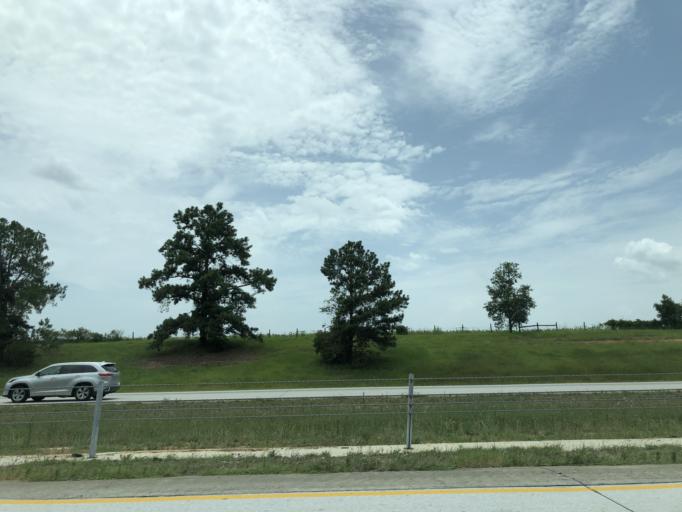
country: US
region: Georgia
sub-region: Evans County
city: Claxton
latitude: 32.3136
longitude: -81.9007
